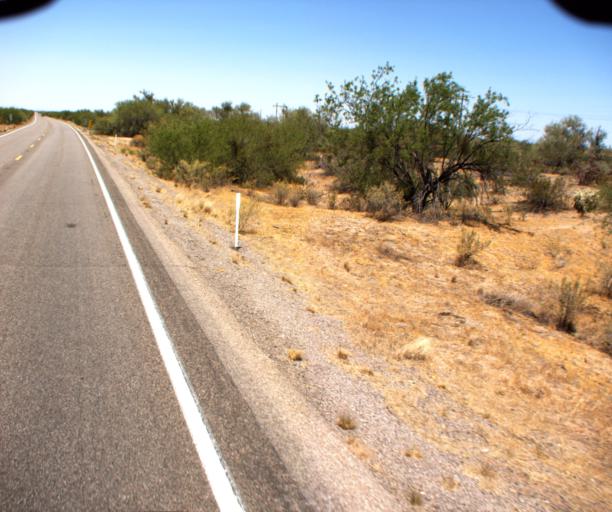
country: US
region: Arizona
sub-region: Pima County
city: Catalina
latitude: 32.7493
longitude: -111.1318
